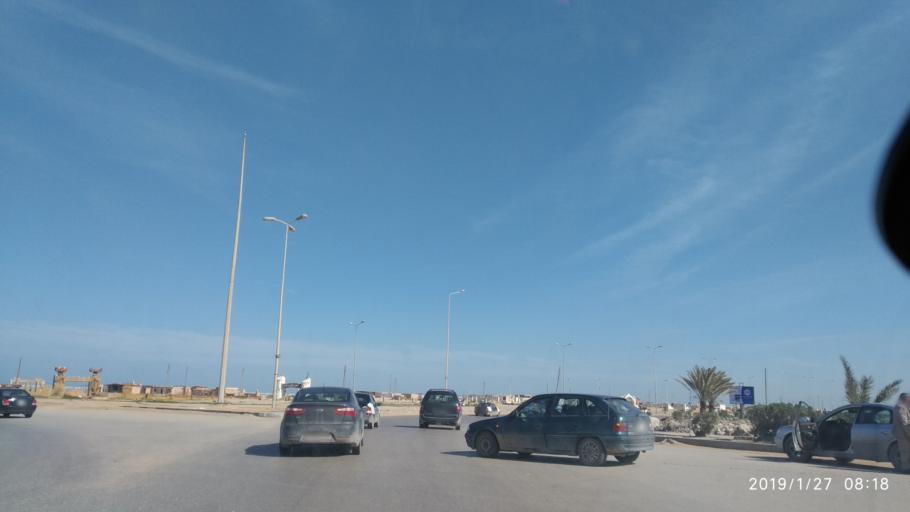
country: LY
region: Tripoli
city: Tagiura
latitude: 32.8953
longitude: 13.3238
